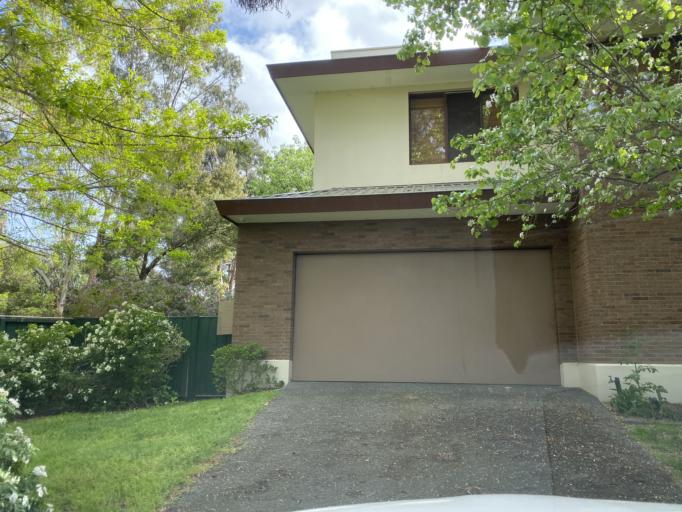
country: AU
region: Victoria
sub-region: Boroondara
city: Canterbury
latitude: -37.8422
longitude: 145.0887
